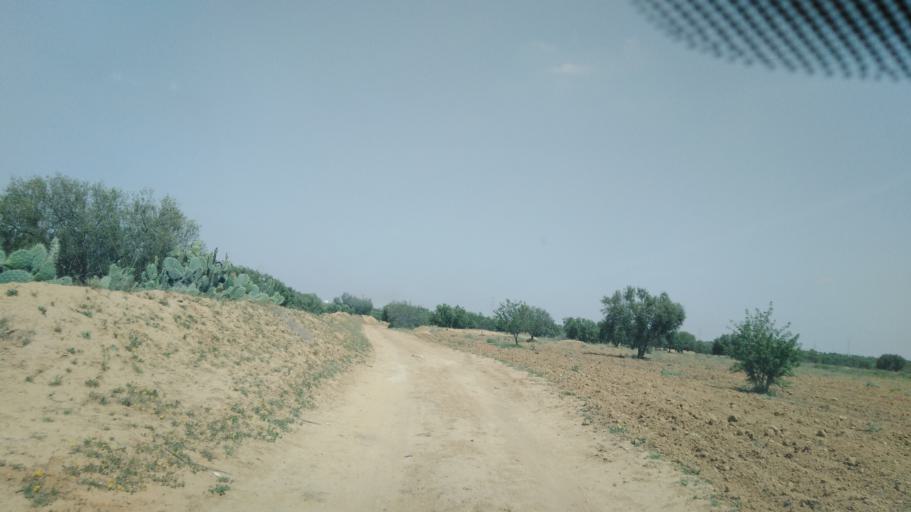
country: TN
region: Safaqis
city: Sfax
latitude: 34.7346
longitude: 10.5746
